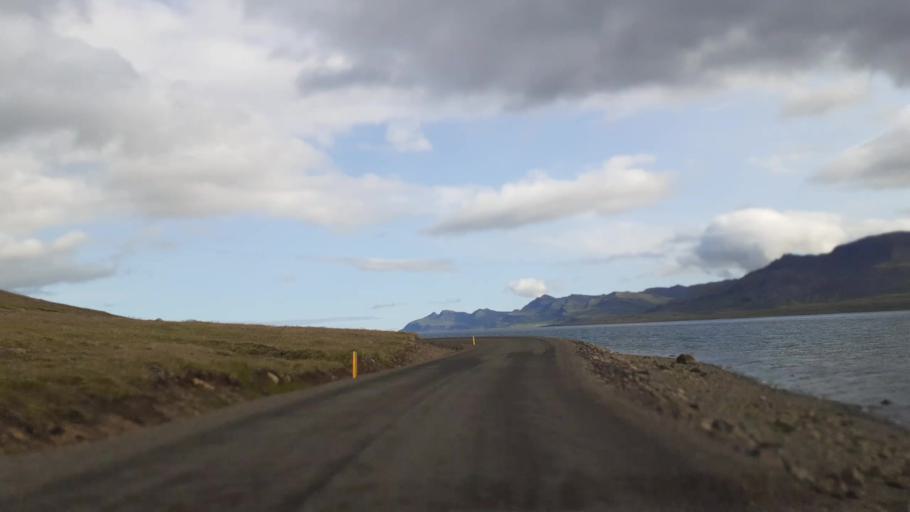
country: IS
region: East
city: Eskifjoerdur
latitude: 65.0575
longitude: -13.9835
